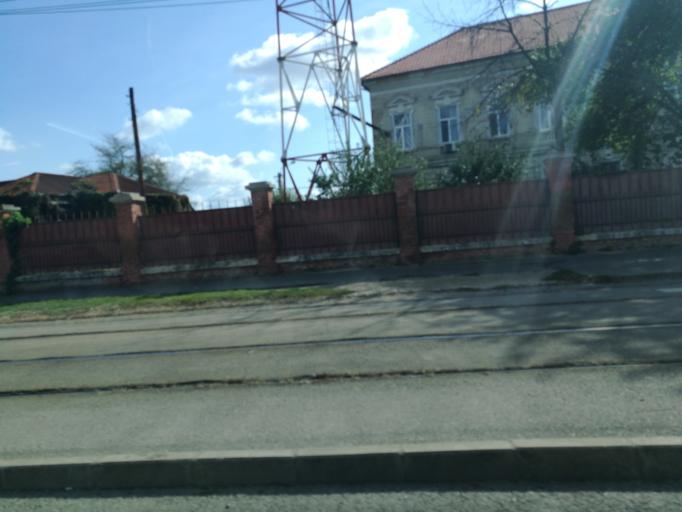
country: RO
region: Bihor
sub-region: Comuna Biharea
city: Oradea
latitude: 47.0558
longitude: 21.9169
